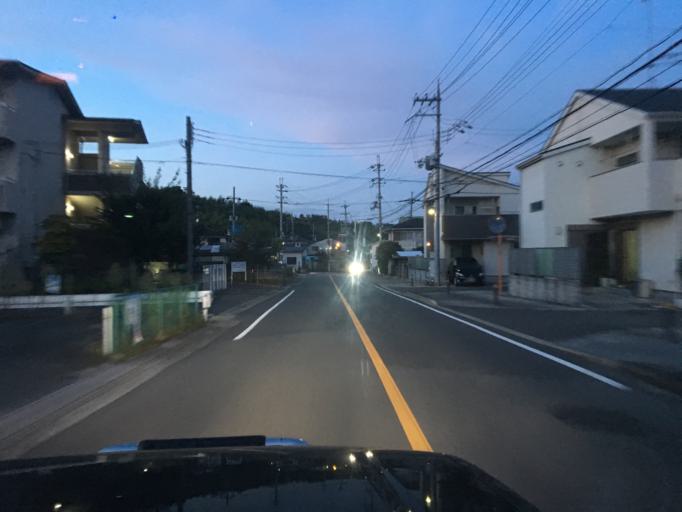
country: JP
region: Kyoto
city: Tanabe
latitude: 34.8151
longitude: 135.7579
